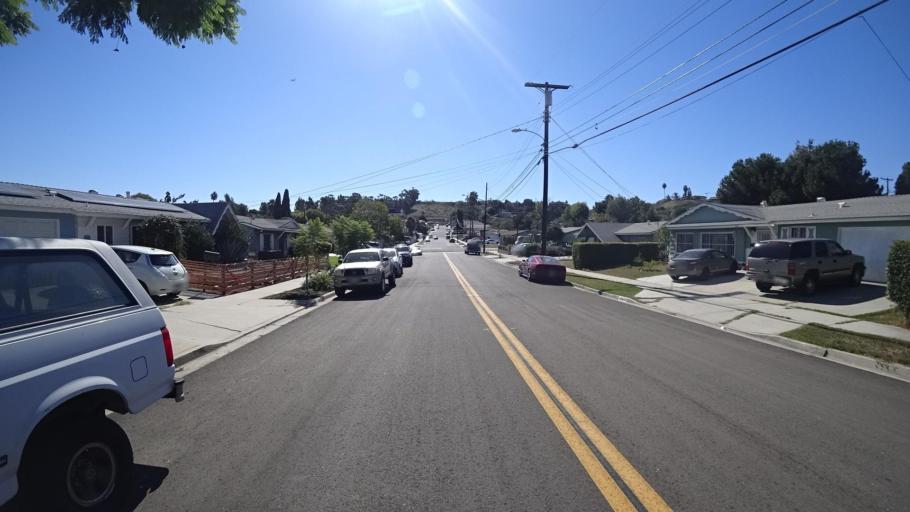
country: US
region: California
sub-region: San Diego County
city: La Presa
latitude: 32.7028
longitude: -117.0174
